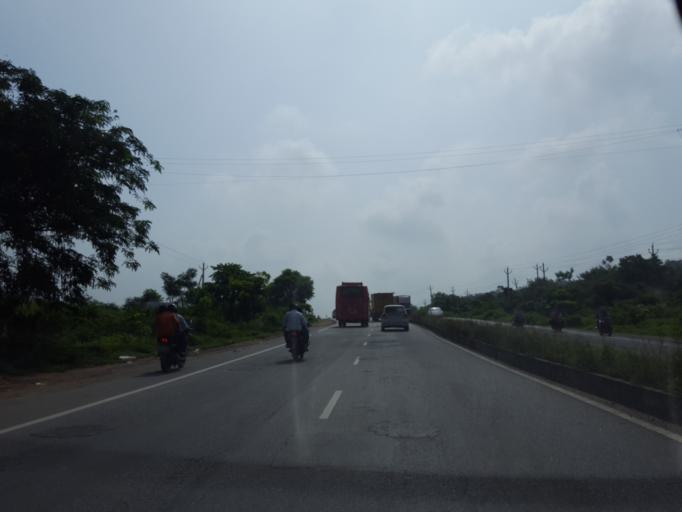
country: IN
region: Telangana
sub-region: Rangareddi
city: Ghatkesar
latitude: 17.2859
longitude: 78.7743
